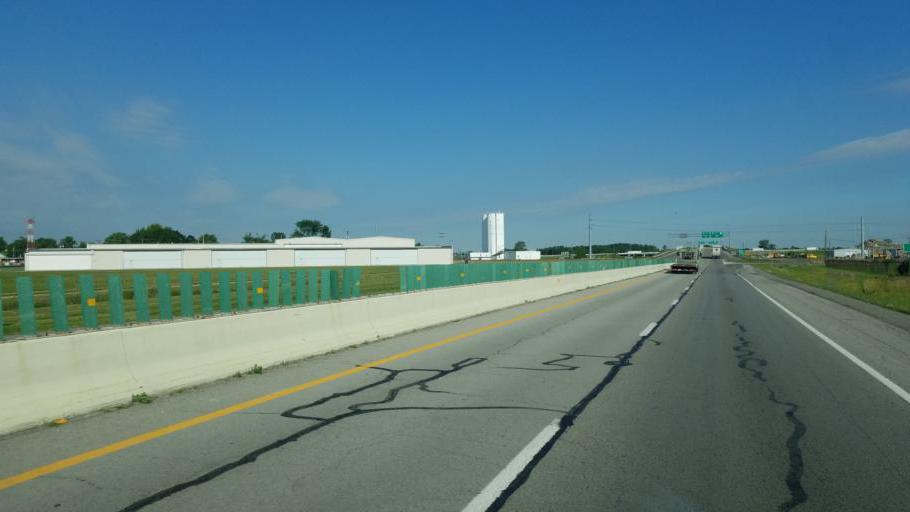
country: US
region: Ohio
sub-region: Hancock County
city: Findlay
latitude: 41.0220
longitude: -83.6649
